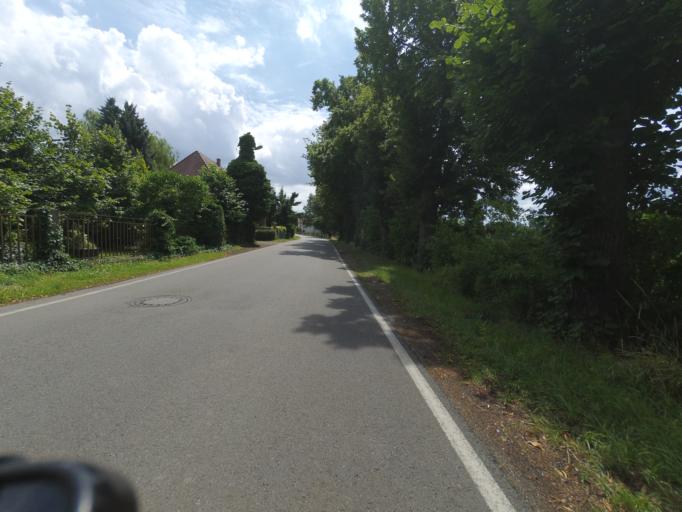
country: DE
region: Saxony
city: Heidenau
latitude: 50.9831
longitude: 13.8859
